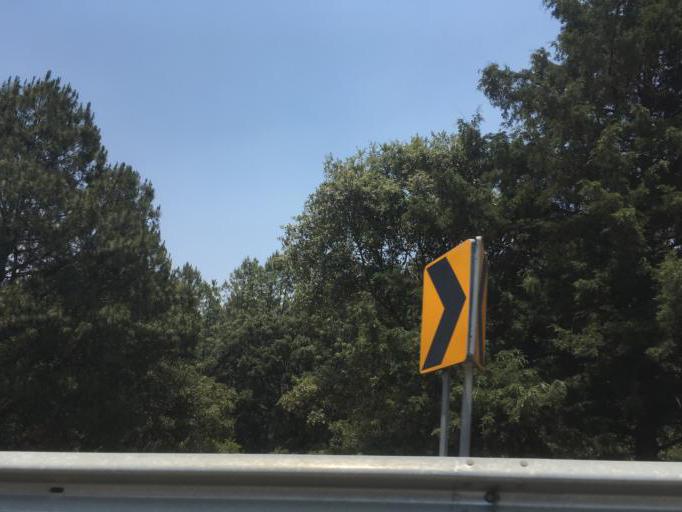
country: MX
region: Michoacan
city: Quiroga
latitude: 19.6379
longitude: -101.4779
